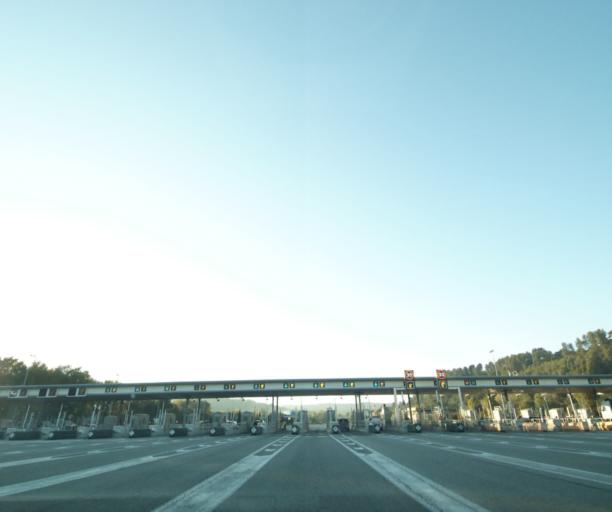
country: FR
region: Provence-Alpes-Cote d'Azur
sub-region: Departement des Bouches-du-Rhone
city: Chateauneuf-le-Rouge
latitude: 43.4828
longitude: 5.5421
